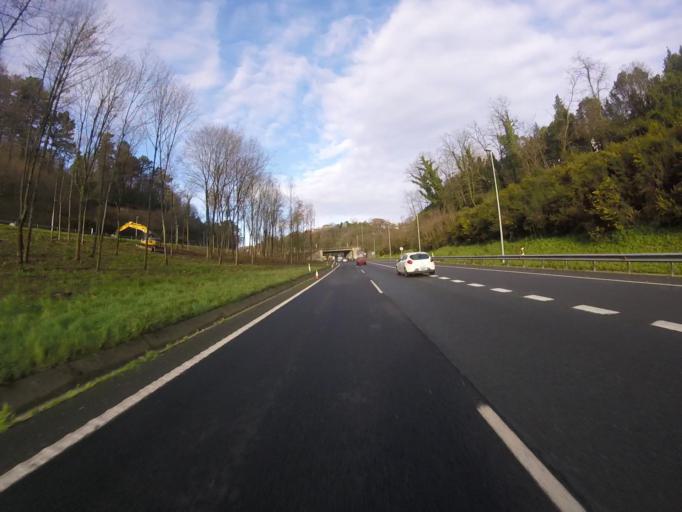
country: ES
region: Basque Country
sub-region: Provincia de Guipuzcoa
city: San Sebastian
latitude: 43.2985
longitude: -1.9784
